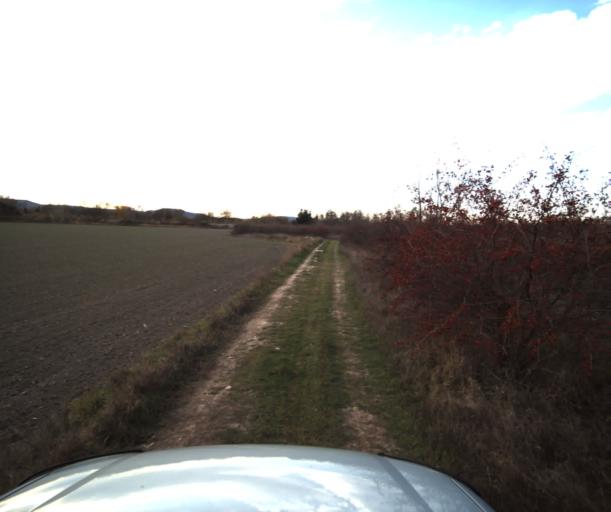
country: FR
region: Provence-Alpes-Cote d'Azur
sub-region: Departement des Bouches-du-Rhone
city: Meyrargues
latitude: 43.6650
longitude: 5.5235
